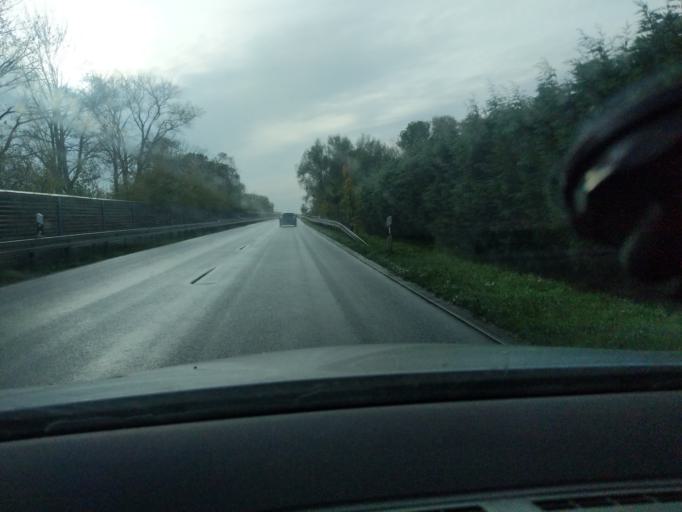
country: DE
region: Lower Saxony
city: Neu Wulmstorf
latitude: 53.5209
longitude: 9.8272
